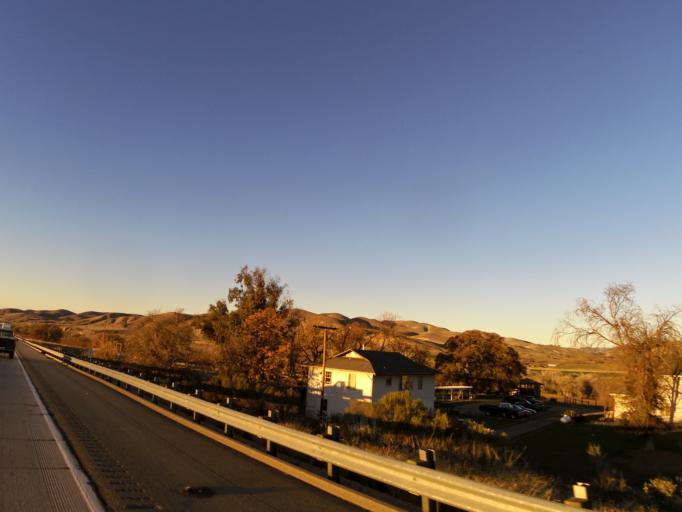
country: US
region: California
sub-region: San Luis Obispo County
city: San Miguel
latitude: 35.7676
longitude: -120.7029
